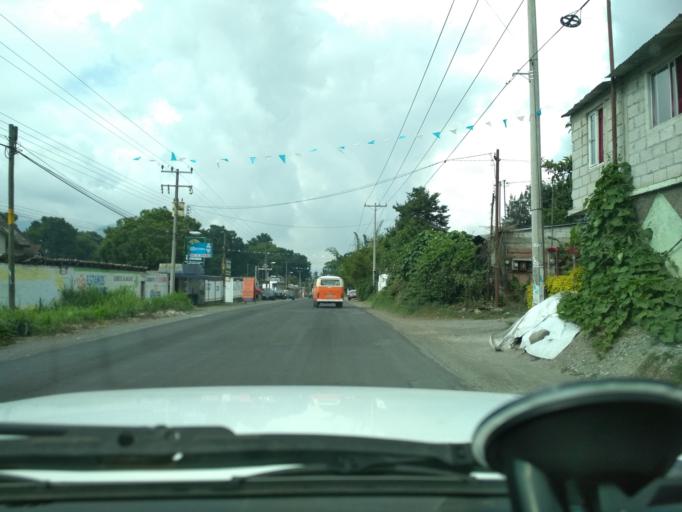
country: MX
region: Veracruz
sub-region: Nogales
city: Taza de Agua Ojo Zarco
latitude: 18.7867
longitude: -97.1998
